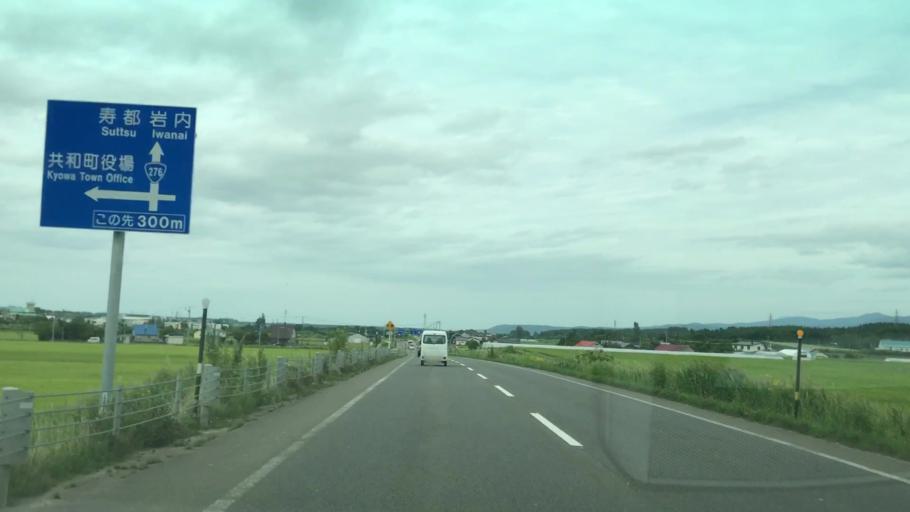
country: JP
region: Hokkaido
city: Iwanai
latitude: 42.9793
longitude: 140.6259
